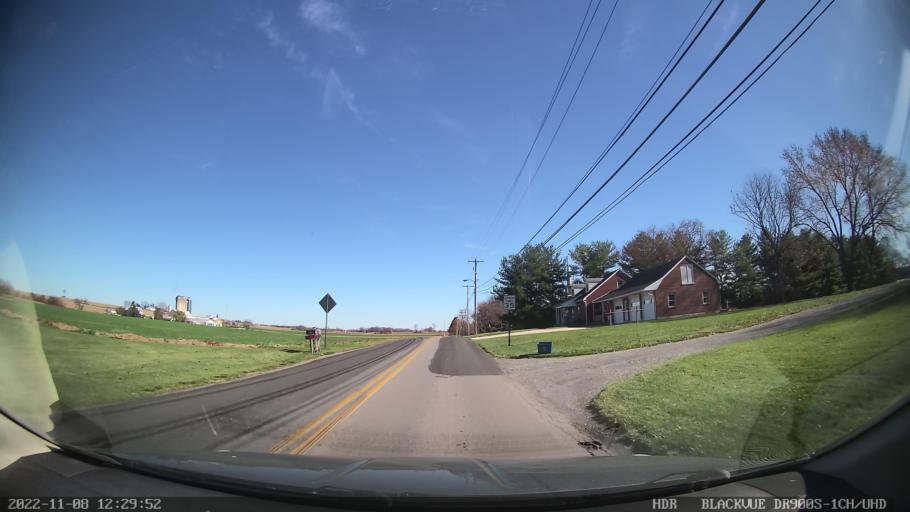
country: US
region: Pennsylvania
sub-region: Berks County
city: Kutztown
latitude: 40.5204
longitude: -75.7582
